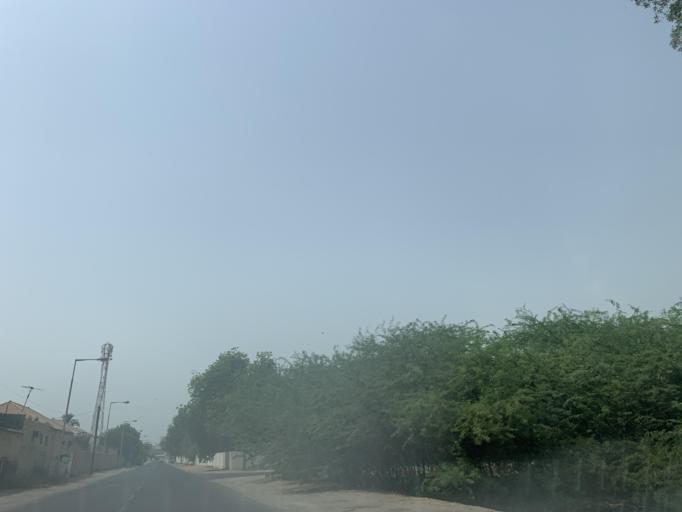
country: BH
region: Manama
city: Jidd Hafs
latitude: 26.2025
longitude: 50.4621
